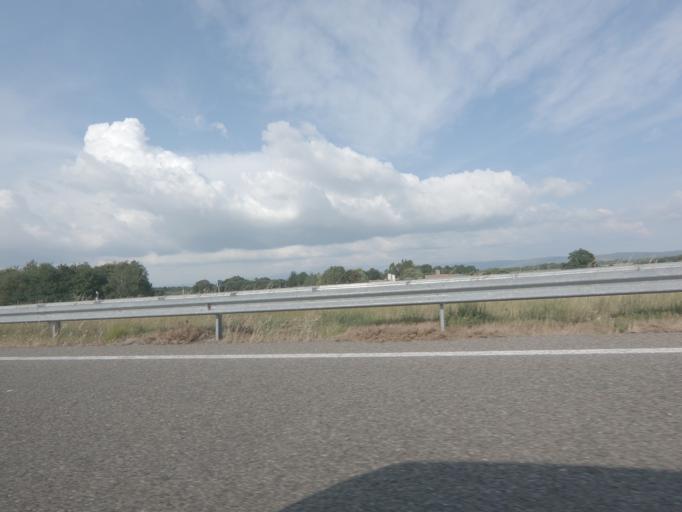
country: ES
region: Galicia
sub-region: Provincia de Ourense
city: Xinzo de Limia
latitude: 42.1212
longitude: -7.7392
